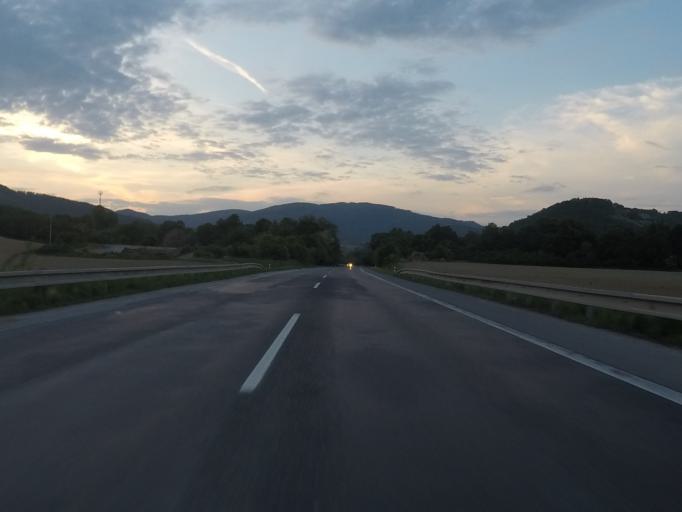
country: SK
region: Banskobystricky
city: Rimavska Sobota
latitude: 48.4903
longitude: 19.9419
